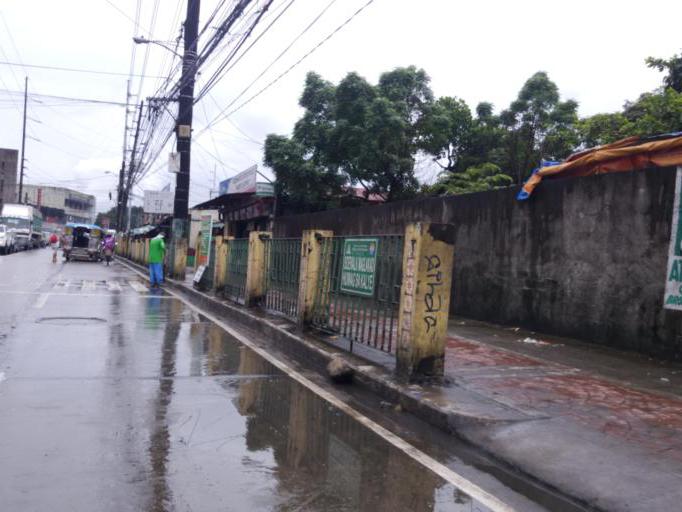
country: PH
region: Calabarzon
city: Bagong Pagasa
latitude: 14.7248
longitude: 121.0413
